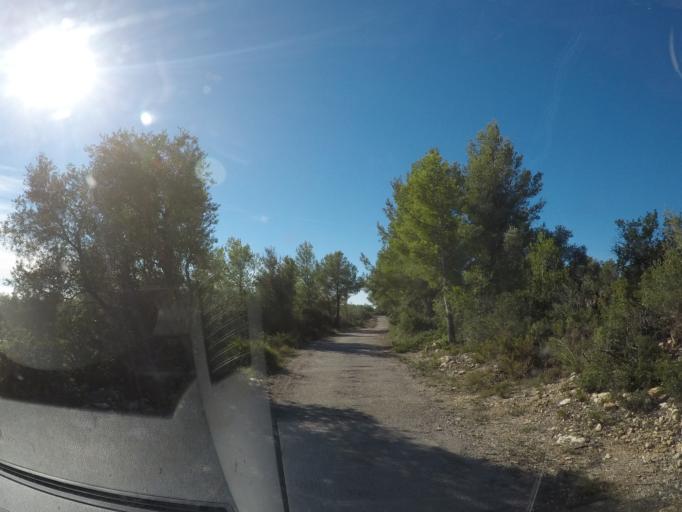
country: ES
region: Catalonia
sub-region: Provincia de Tarragona
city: El Perello
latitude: 40.9147
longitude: 0.7232
